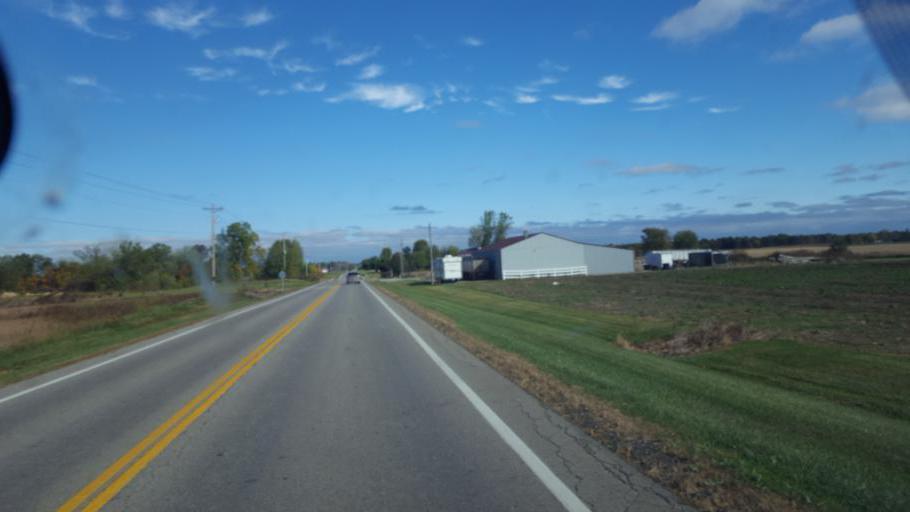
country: US
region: Ohio
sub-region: Huron County
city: Greenwich
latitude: 41.0535
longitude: -82.4862
